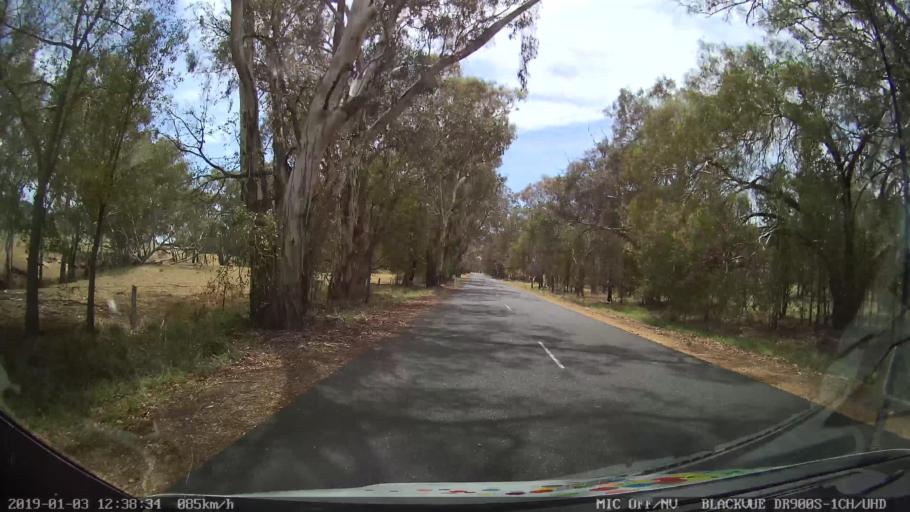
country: AU
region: New South Wales
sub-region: Weddin
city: Grenfell
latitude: -33.8324
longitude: 148.1971
